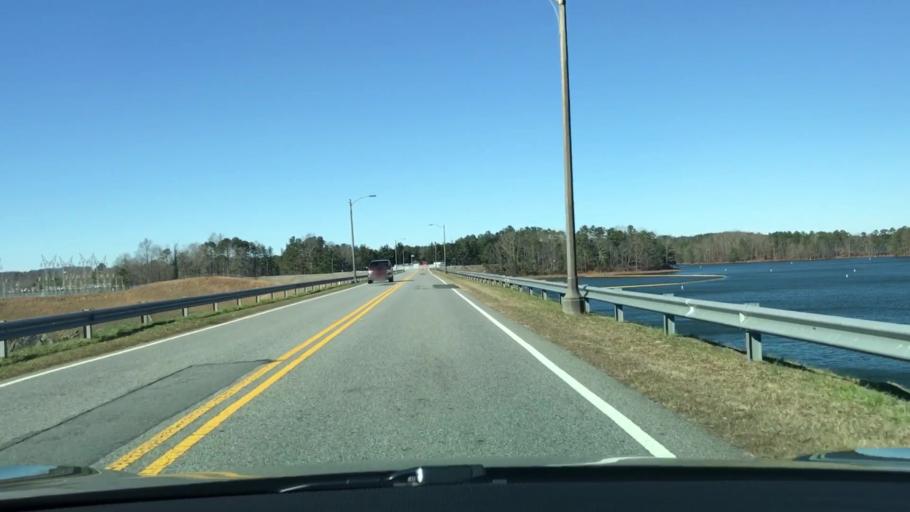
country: US
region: Georgia
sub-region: Gwinnett County
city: Sugar Hill
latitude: 34.1596
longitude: -84.0730
